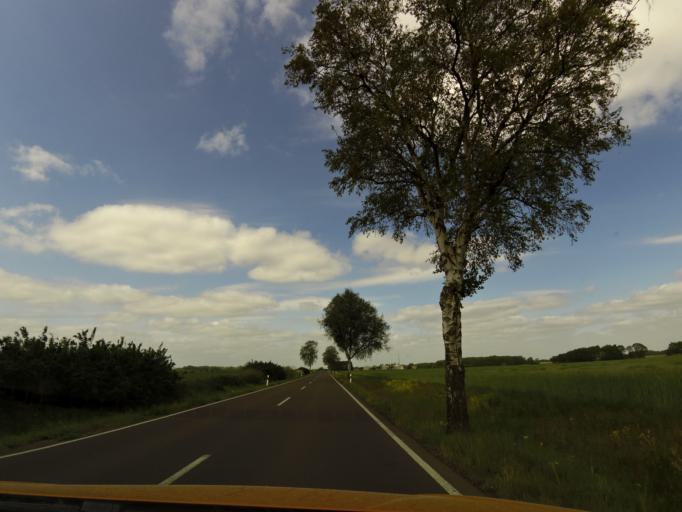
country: DE
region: Saxony-Anhalt
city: Loburg
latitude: 52.1103
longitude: 12.1215
